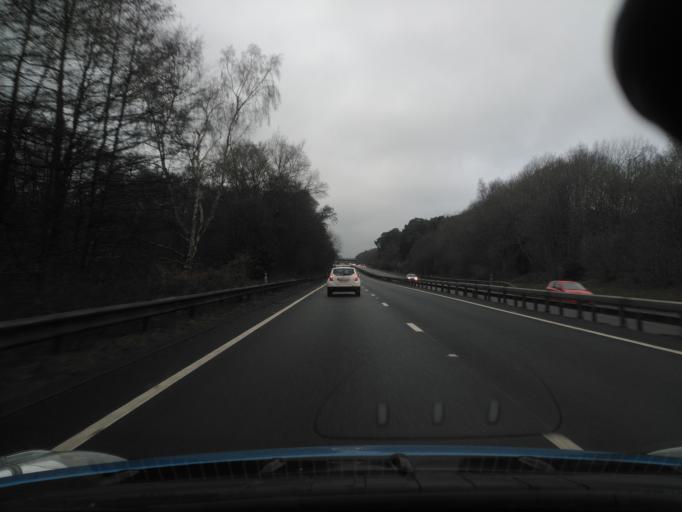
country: GB
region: England
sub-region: Surrey
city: Elstead
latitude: 51.1545
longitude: -0.6877
